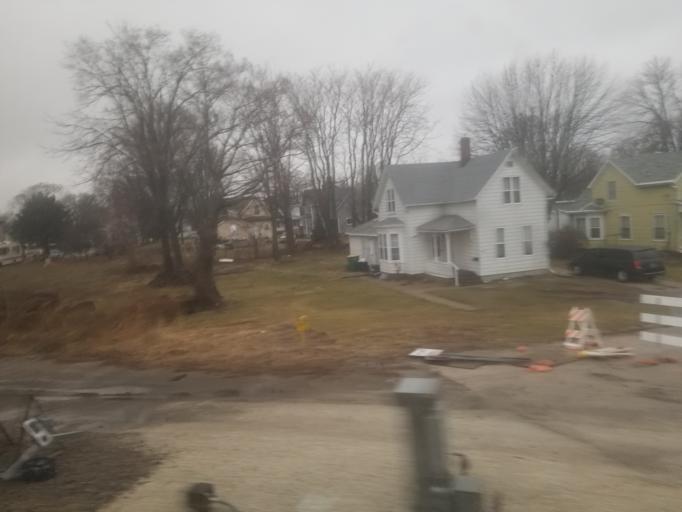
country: US
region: Illinois
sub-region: Knox County
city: Galesburg
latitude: 40.9491
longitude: -90.3586
